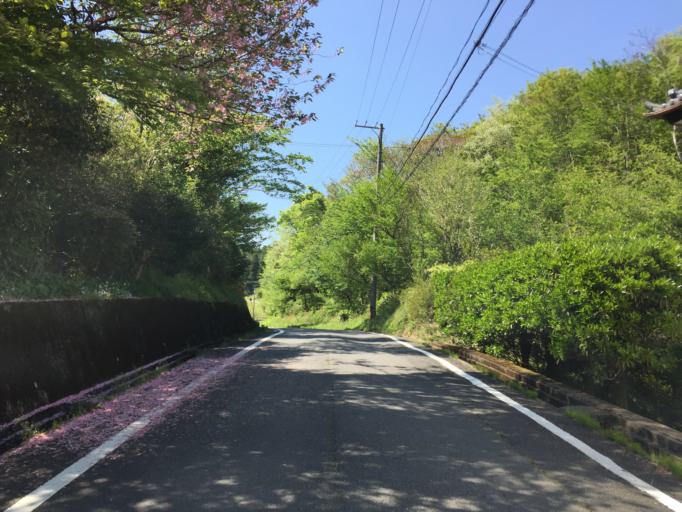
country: JP
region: Fukushima
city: Iwaki
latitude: 37.0550
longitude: 140.7959
